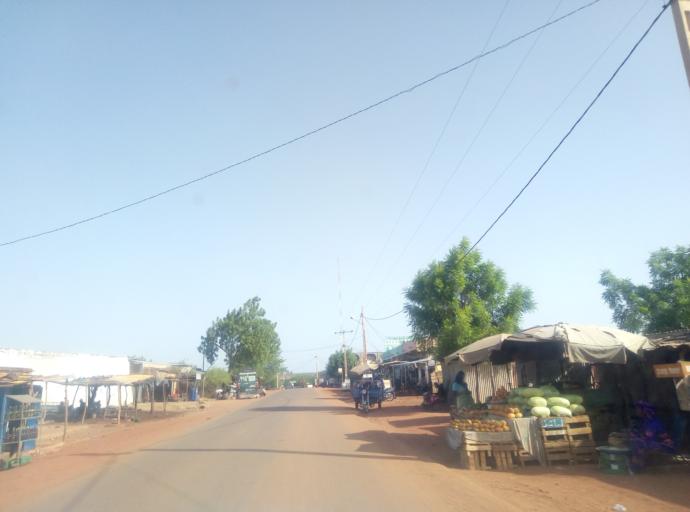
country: ML
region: Bamako
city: Bamako
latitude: 12.6140
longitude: -7.7771
